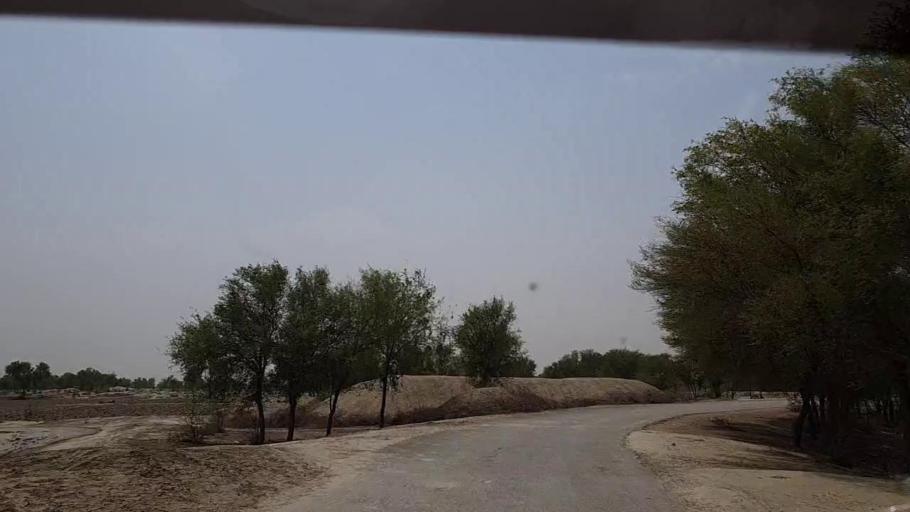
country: PK
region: Sindh
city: Khairpur Nathan Shah
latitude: 27.0170
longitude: 67.5935
